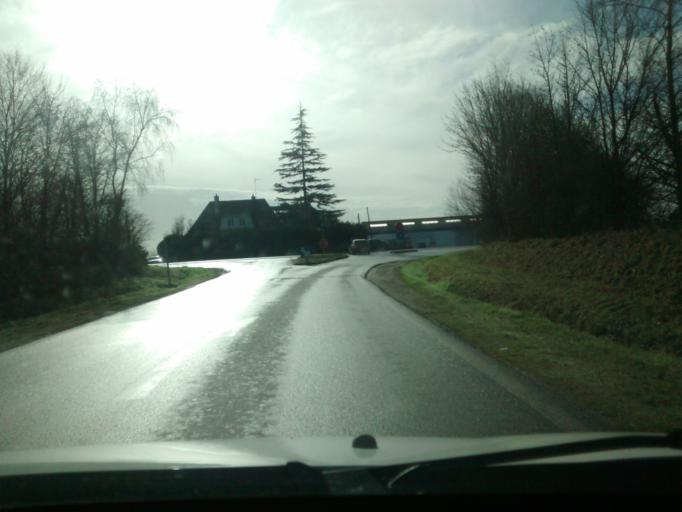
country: FR
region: Brittany
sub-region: Departement d'Ille-et-Vilaine
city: Vezin-le-Coquet
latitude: 48.1185
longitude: -1.7351
